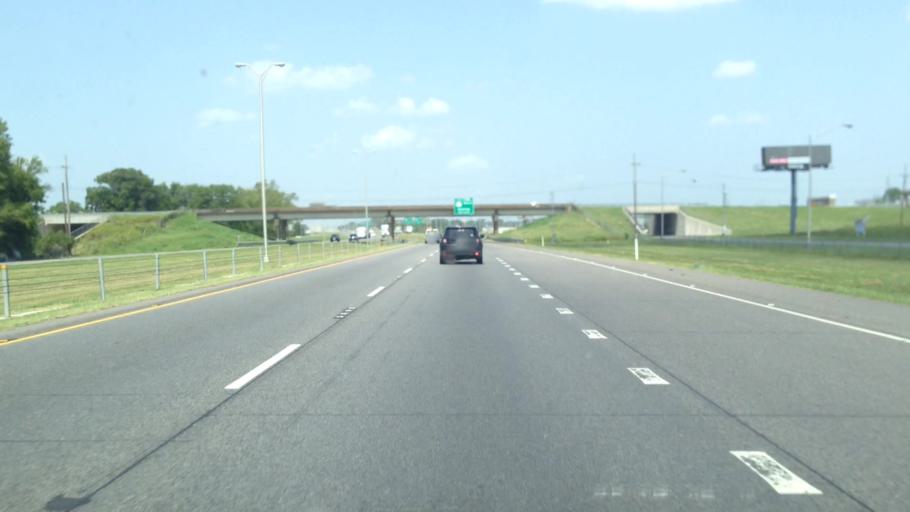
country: US
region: Louisiana
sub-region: Ouachita Parish
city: Monroe
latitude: 32.4982
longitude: -92.0734
